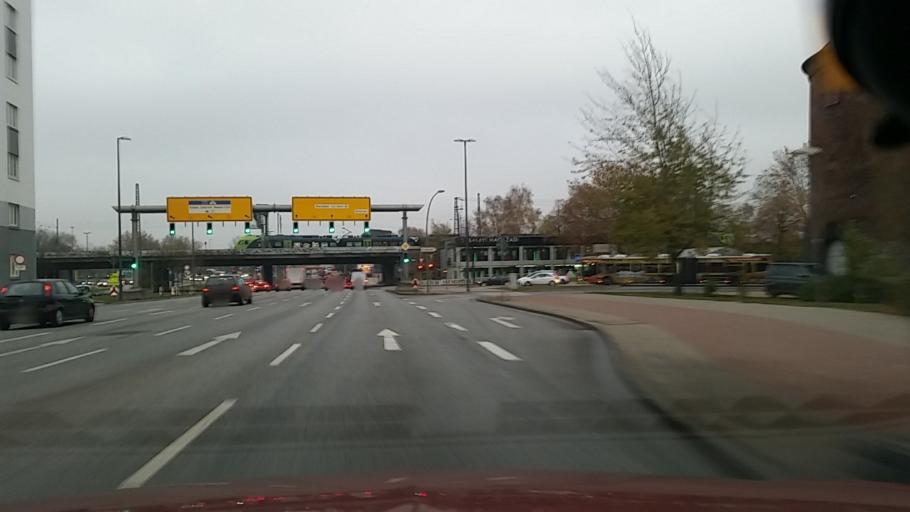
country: DE
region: Hamburg
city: Hammerbrook
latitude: 53.5384
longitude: 10.0318
